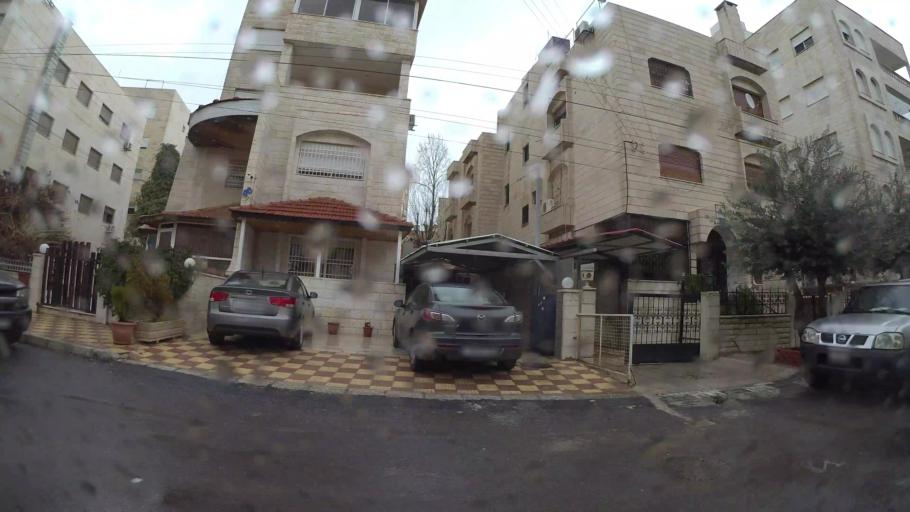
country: JO
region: Amman
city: Wadi as Sir
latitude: 31.9723
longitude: 35.8464
